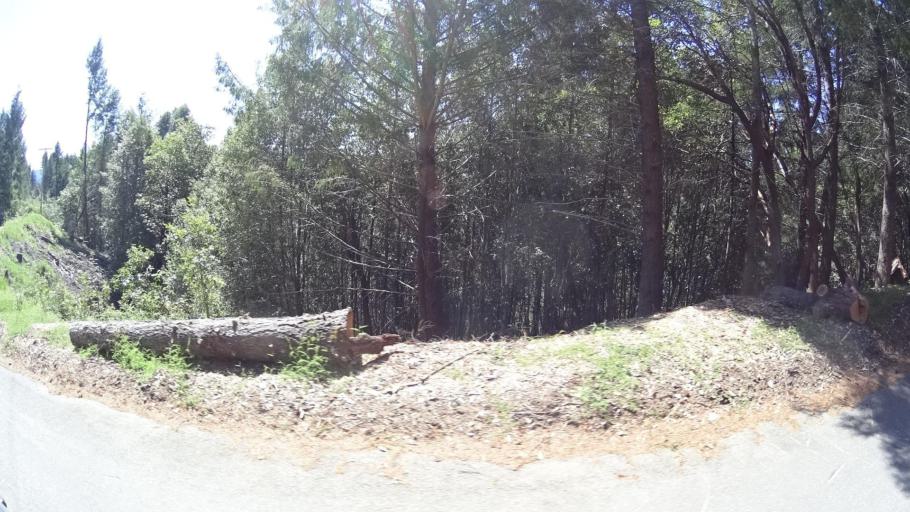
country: US
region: California
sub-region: Humboldt County
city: Redway
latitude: 40.1509
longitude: -124.0282
